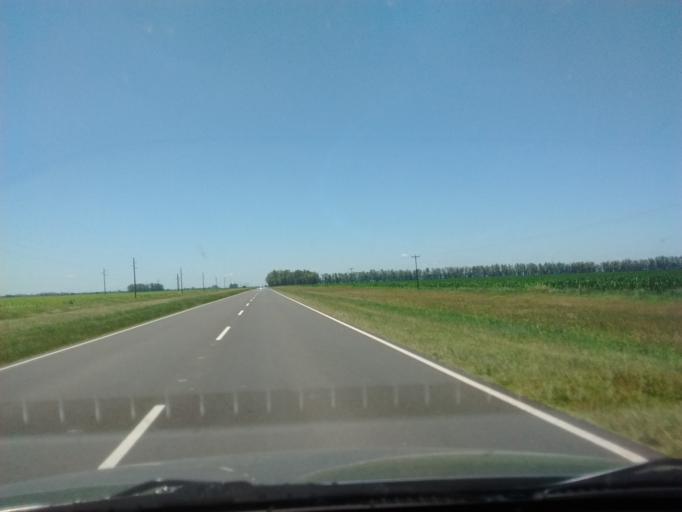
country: AR
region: Entre Rios
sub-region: Departamento de Gualeguay
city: Gualeguay
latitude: -32.9973
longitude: -59.5166
